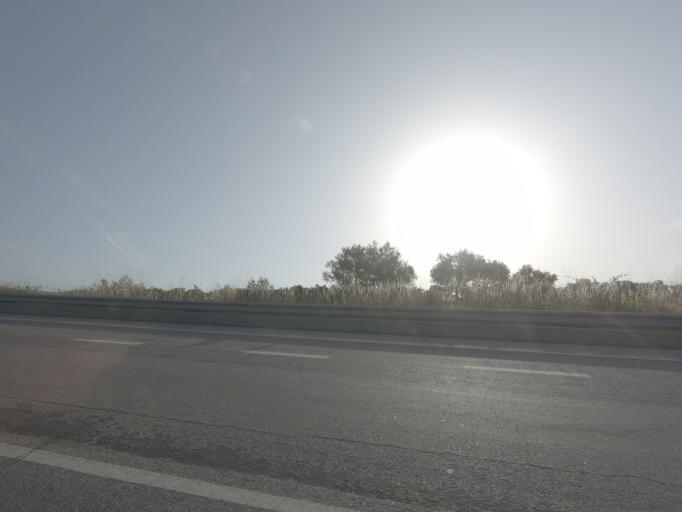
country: PT
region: Vila Real
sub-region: Sabrosa
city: Sabrosa
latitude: 41.2813
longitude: -7.4718
